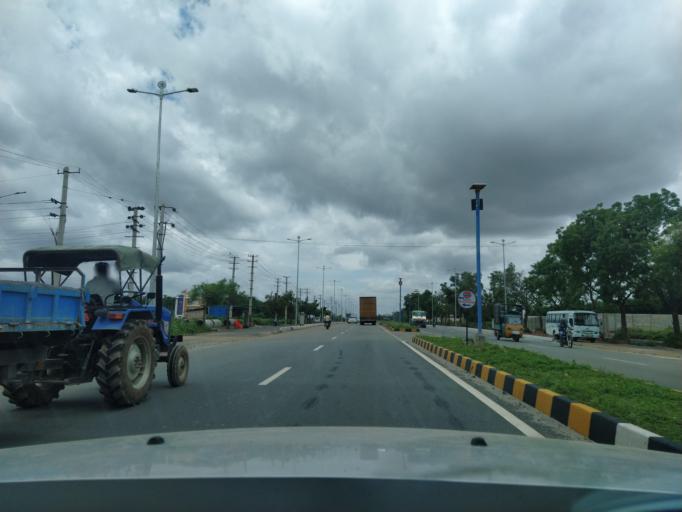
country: IN
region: Karnataka
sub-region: Tumkur
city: Tumkur
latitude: 13.3100
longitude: 77.1346
